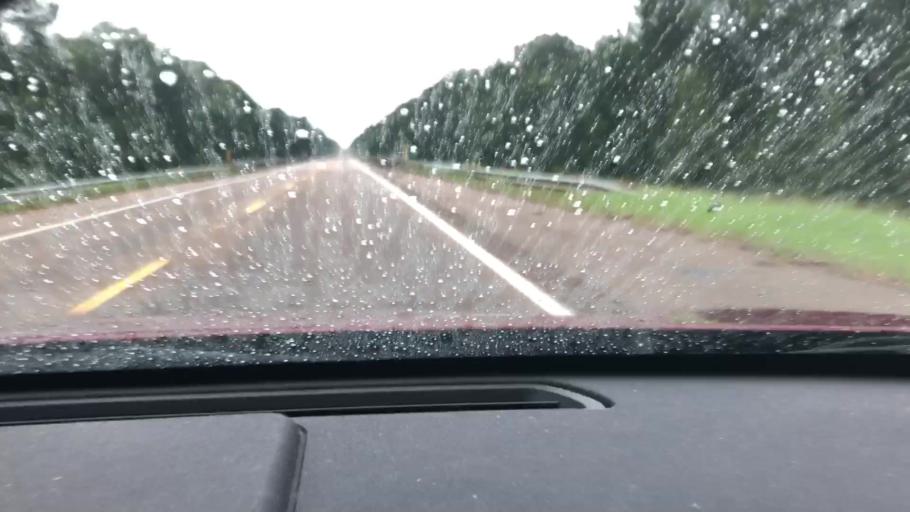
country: US
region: Arkansas
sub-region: Columbia County
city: Magnolia
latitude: 33.3025
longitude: -93.2692
